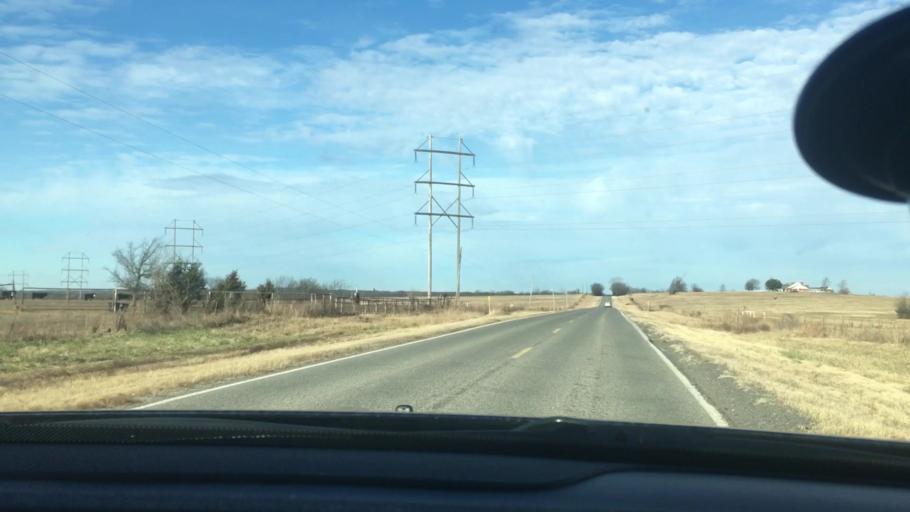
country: US
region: Oklahoma
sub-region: Seminole County
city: Konawa
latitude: 34.9742
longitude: -96.7823
